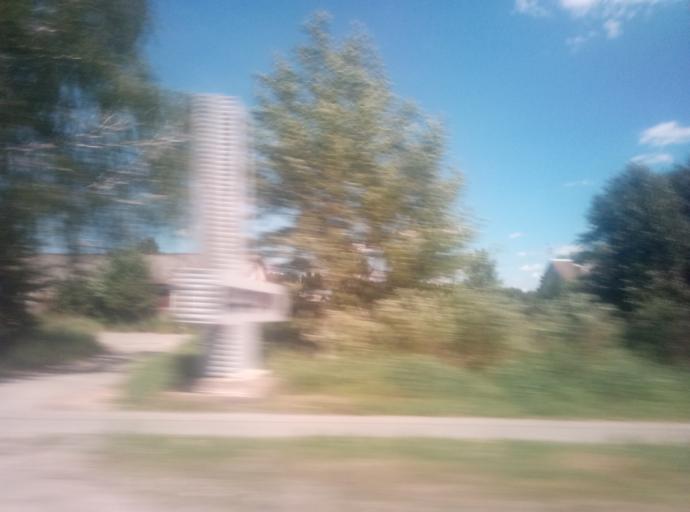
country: RU
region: Tula
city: Kireyevsk
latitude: 54.0167
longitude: 37.9148
